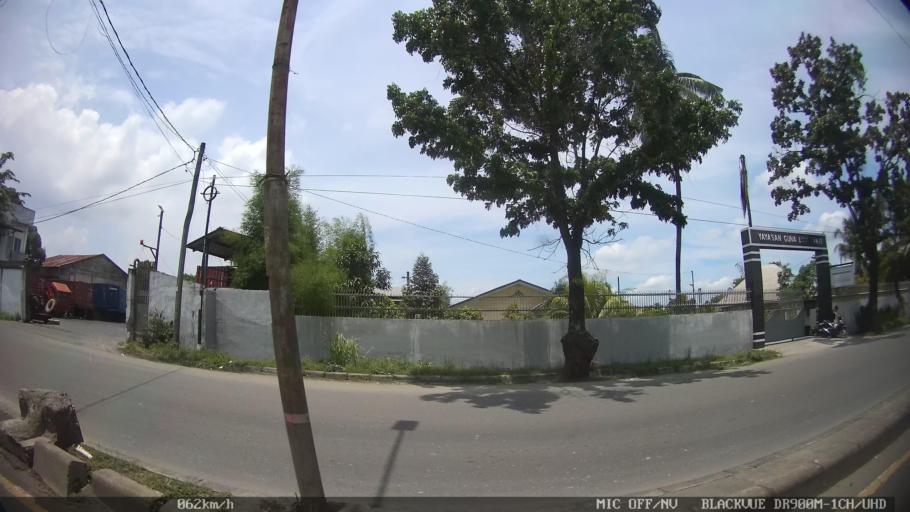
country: ID
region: North Sumatra
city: Labuhan Deli
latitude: 3.7168
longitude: 98.6798
